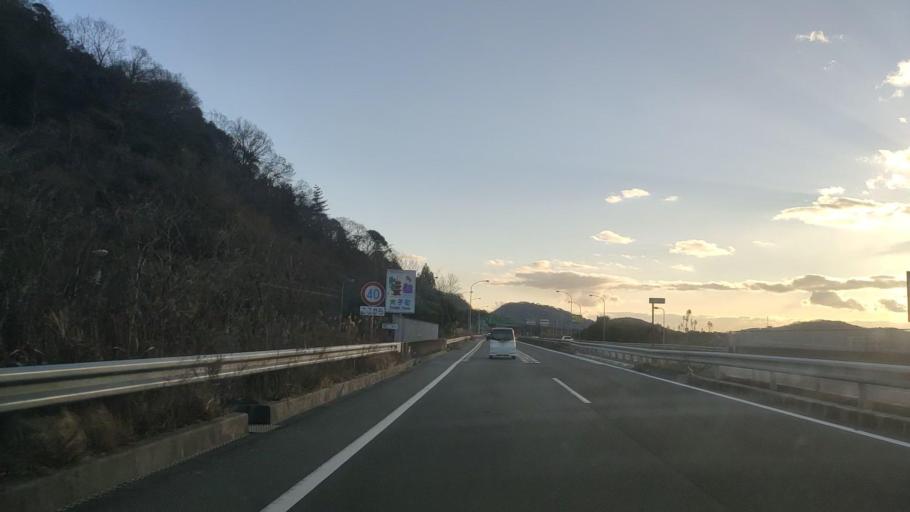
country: JP
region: Hyogo
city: Tatsunocho-tominaga
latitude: 34.8513
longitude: 134.6048
